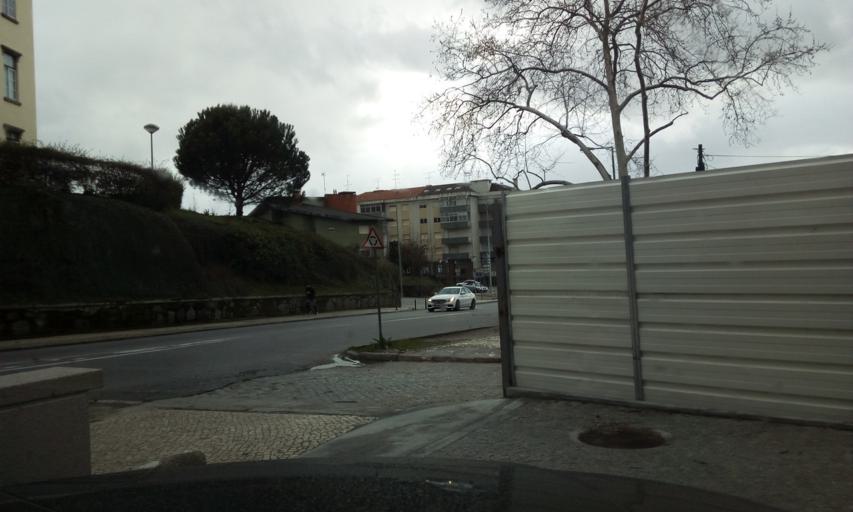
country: PT
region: Viseu
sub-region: Viseu
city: Viseu
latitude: 40.6567
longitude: -7.9048
